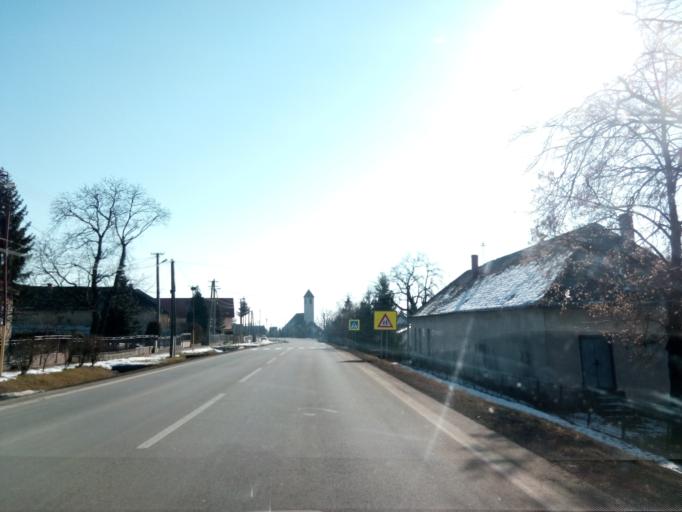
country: SK
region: Kosicky
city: Secovce
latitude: 48.7323
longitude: 21.5831
